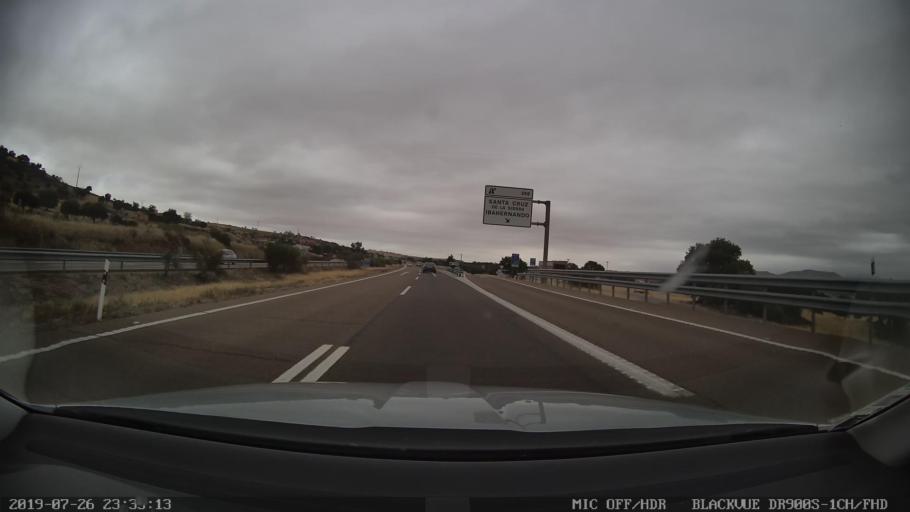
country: ES
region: Extremadura
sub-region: Provincia de Caceres
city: Santa Cruz de la Sierra
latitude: 39.3353
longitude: -5.8564
